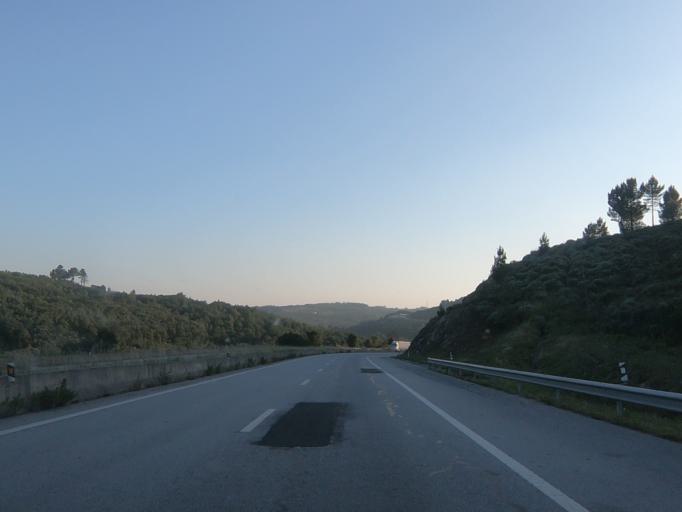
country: PT
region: Guarda
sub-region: Fornos de Algodres
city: Fornos de Algodres
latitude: 40.6317
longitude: -7.4679
